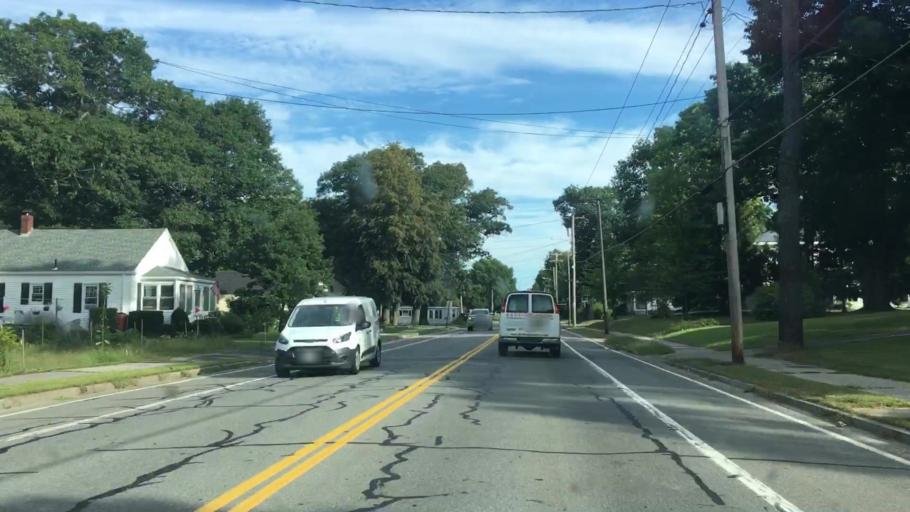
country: US
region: Maine
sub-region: Cumberland County
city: Falmouth
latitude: 43.7138
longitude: -70.2919
